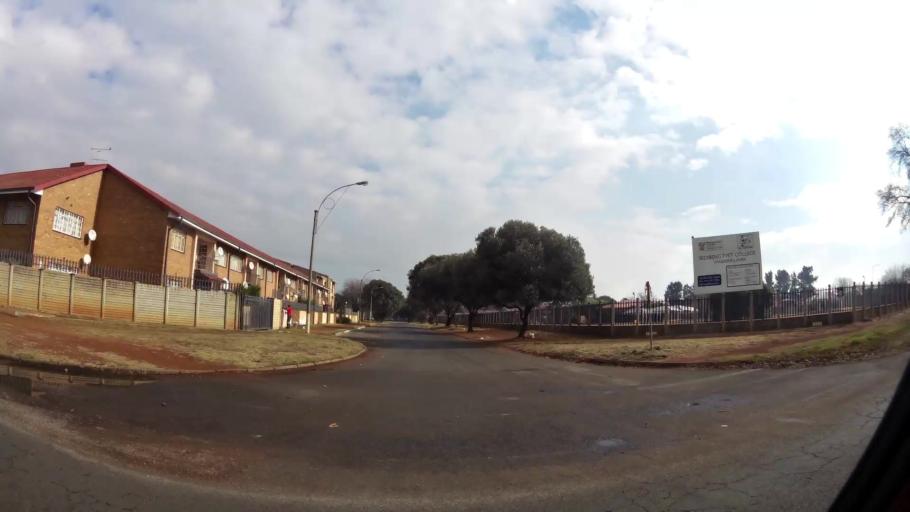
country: ZA
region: Gauteng
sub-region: Sedibeng District Municipality
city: Vanderbijlpark
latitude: -26.6937
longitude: 27.8347
